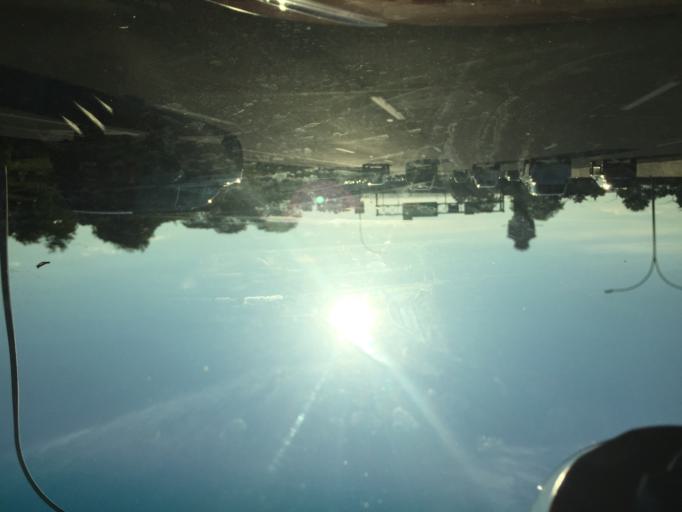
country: US
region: New York
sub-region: Queens County
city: Long Island City
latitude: 40.7705
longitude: -73.8789
